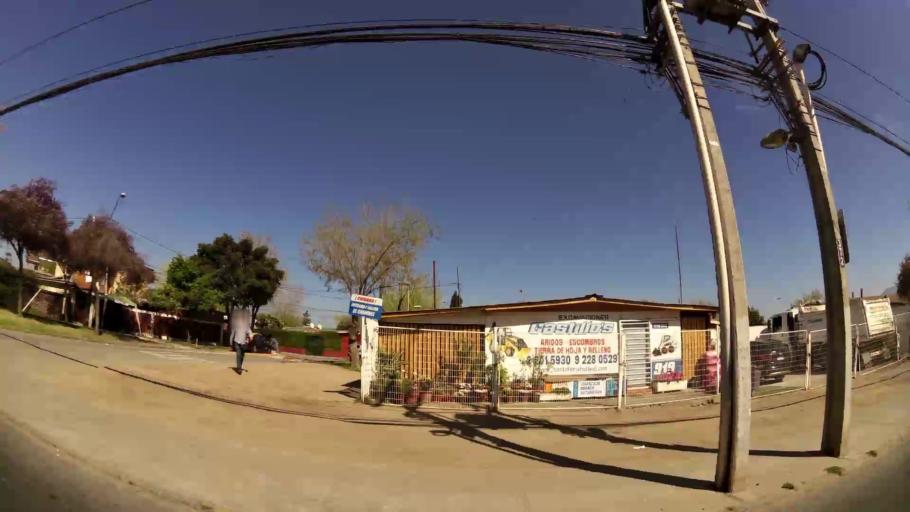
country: CL
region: Santiago Metropolitan
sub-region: Provincia de Santiago
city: Villa Presidente Frei, Nunoa, Santiago, Chile
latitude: -33.4146
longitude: -70.5345
